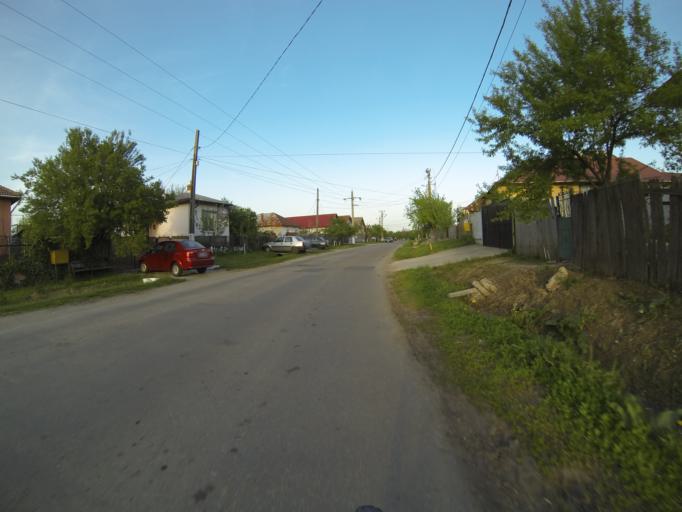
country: RO
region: Dolj
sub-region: Comuna Pielesti
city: Pielesti
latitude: 44.3491
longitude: 23.9091
